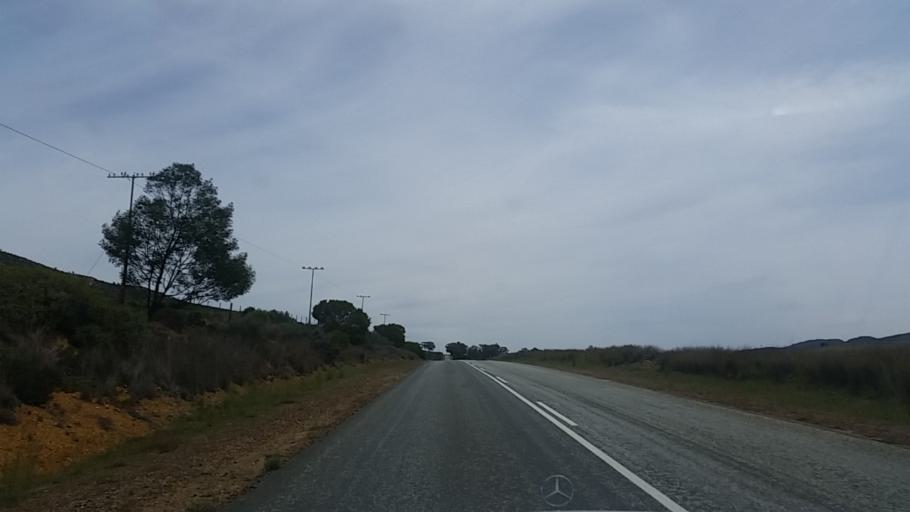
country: ZA
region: Western Cape
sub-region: Eden District Municipality
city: Knysna
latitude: -33.7726
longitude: 22.9353
